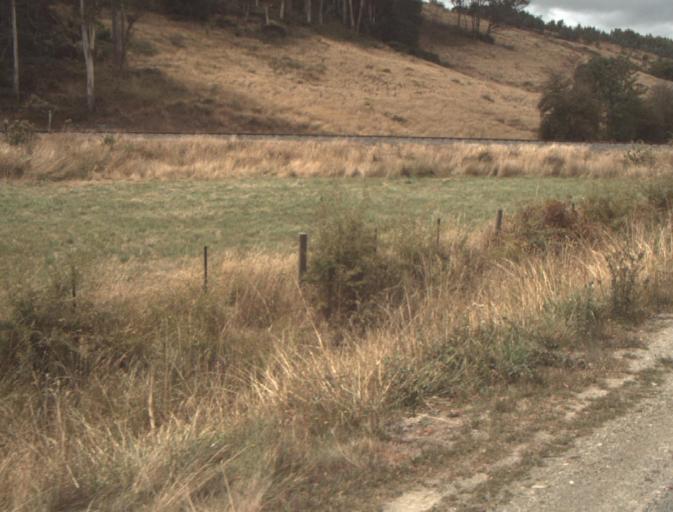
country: AU
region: Tasmania
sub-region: Launceston
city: Mayfield
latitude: -41.2340
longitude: 147.2117
